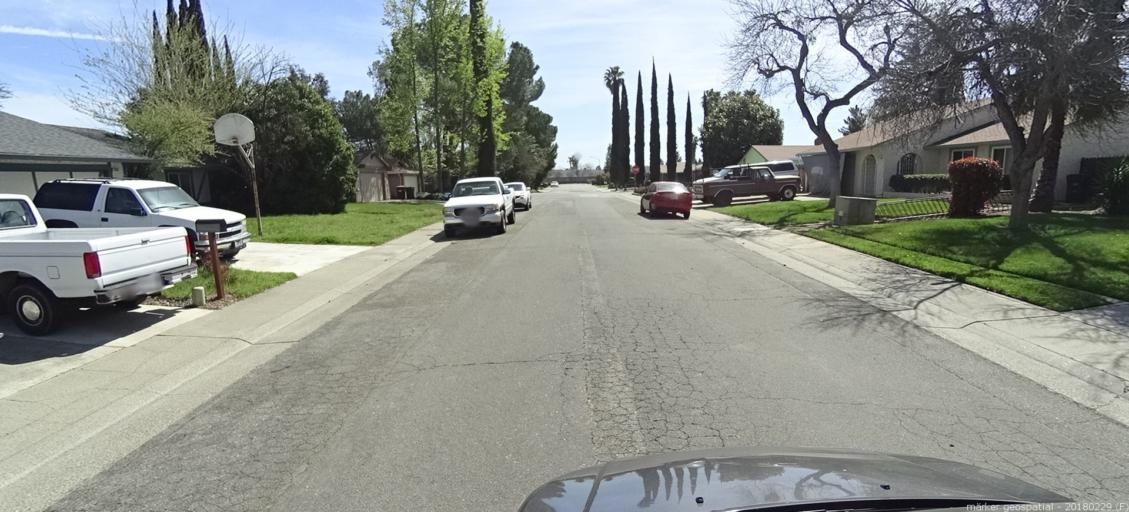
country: US
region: California
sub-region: Sacramento County
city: Rosemont
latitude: 38.5418
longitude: -121.3556
